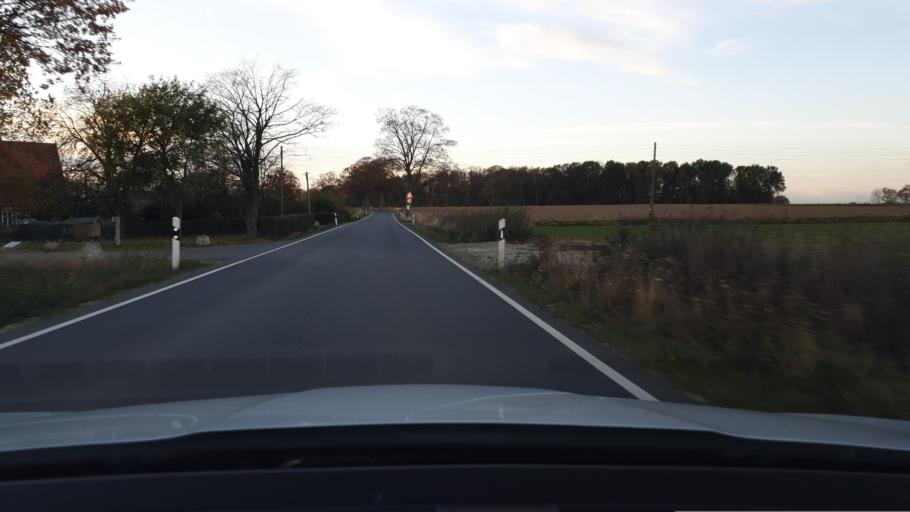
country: DE
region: North Rhine-Westphalia
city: Spenge
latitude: 52.1014
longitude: 8.4938
